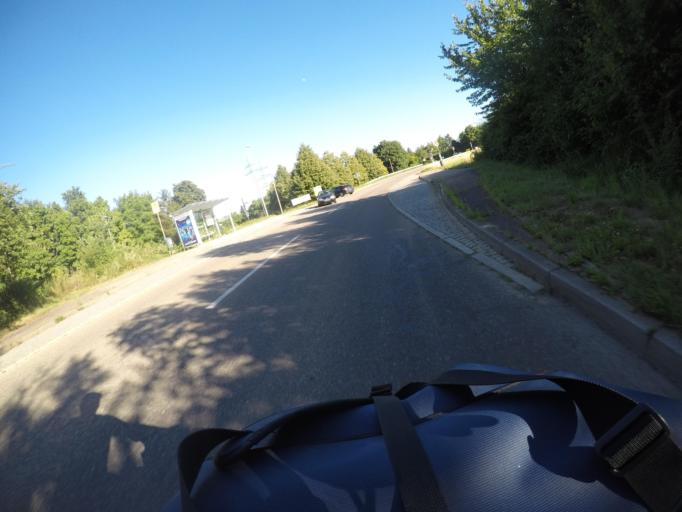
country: DE
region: Baden-Wuerttemberg
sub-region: Regierungsbezirk Stuttgart
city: Stuttgart Muehlhausen
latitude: 48.8880
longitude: 9.2397
